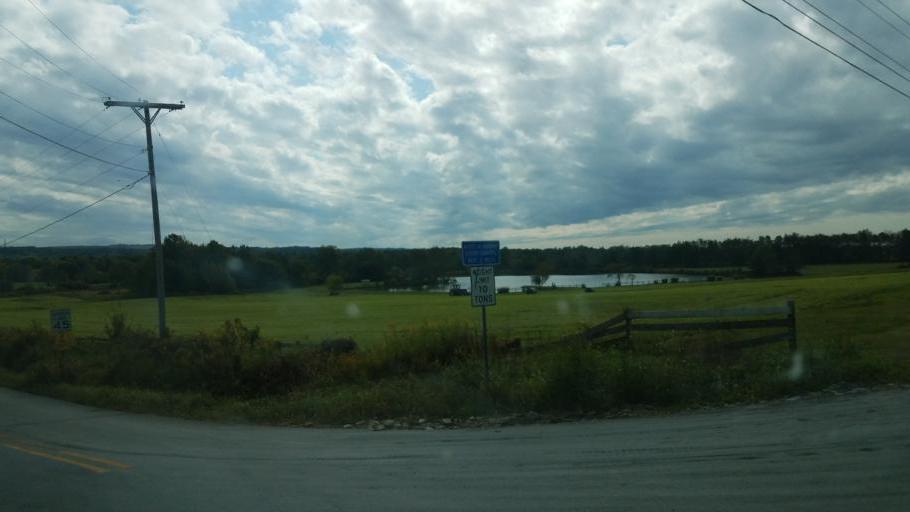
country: US
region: Pennsylvania
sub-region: Mercer County
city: Greenville
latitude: 41.5057
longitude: -80.3691
